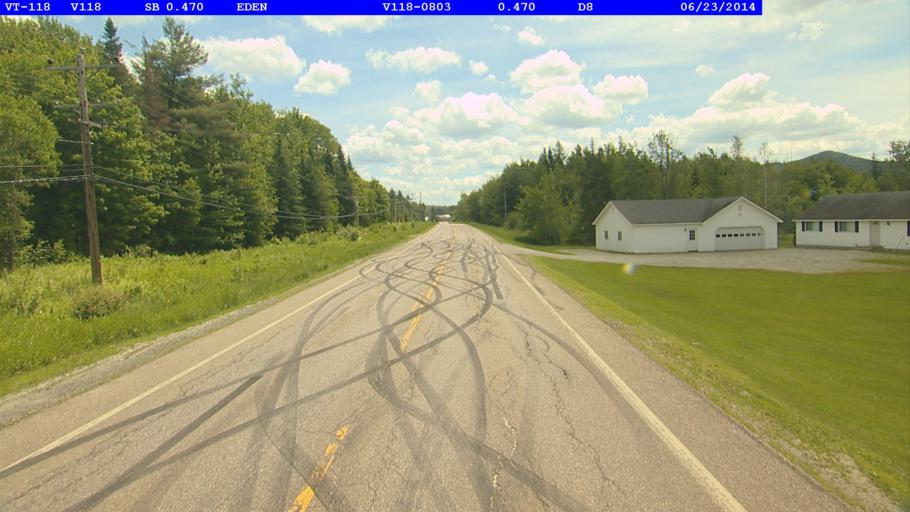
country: US
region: Vermont
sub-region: Lamoille County
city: Hyde Park
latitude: 44.7127
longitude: -72.5513
